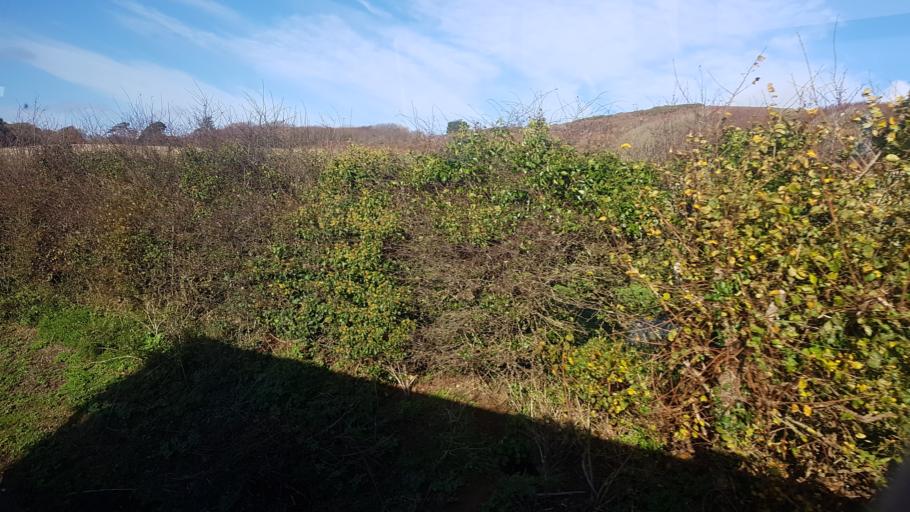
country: GB
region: England
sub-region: Isle of Wight
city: Shalfleet
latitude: 50.6506
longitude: -1.4222
